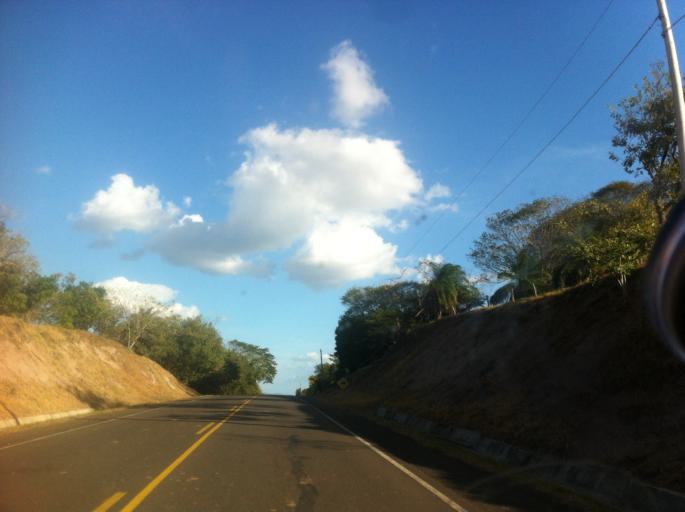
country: NI
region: Chontales
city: Acoyapa
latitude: 11.8566
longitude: -85.0587
